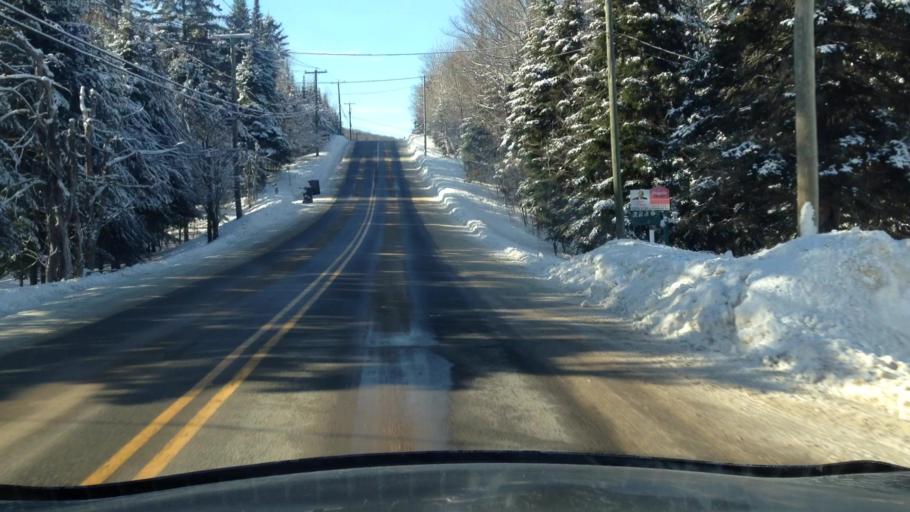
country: CA
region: Quebec
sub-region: Laurentides
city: Sainte-Agathe-des-Monts
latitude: 45.9310
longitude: -74.4234
